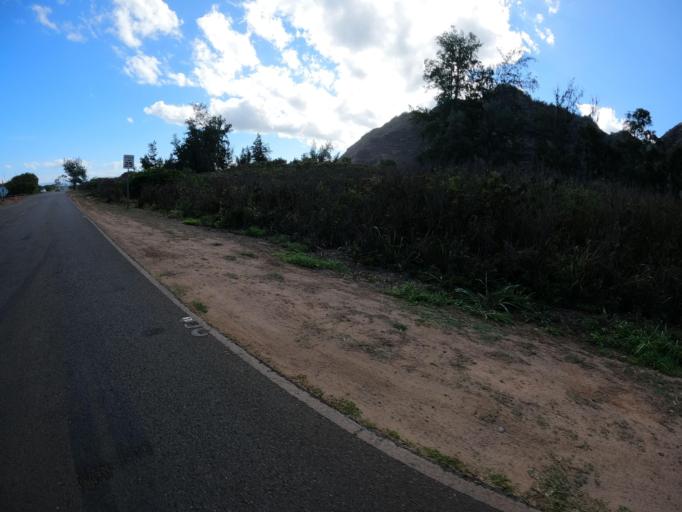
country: US
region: Hawaii
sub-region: Honolulu County
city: Mokuleia
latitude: 21.5786
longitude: -158.2175
